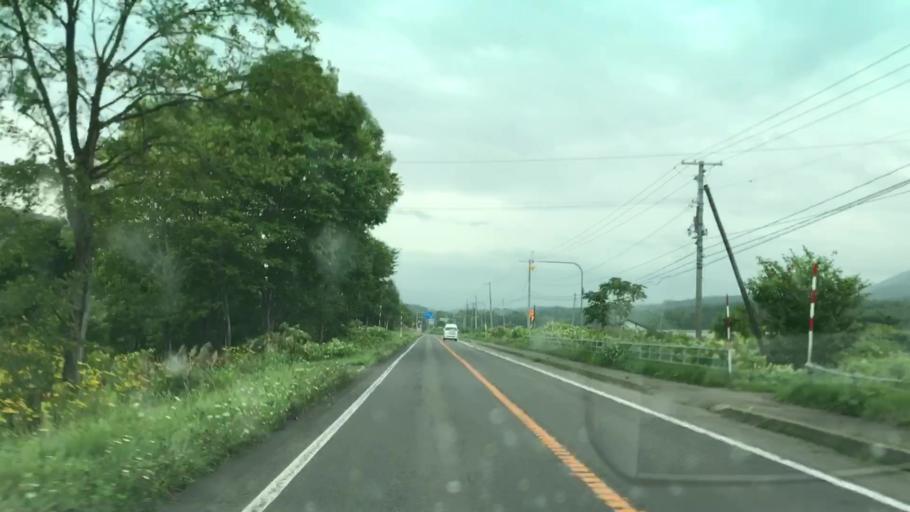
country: JP
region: Hokkaido
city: Niseko Town
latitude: 42.7672
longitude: 140.4844
